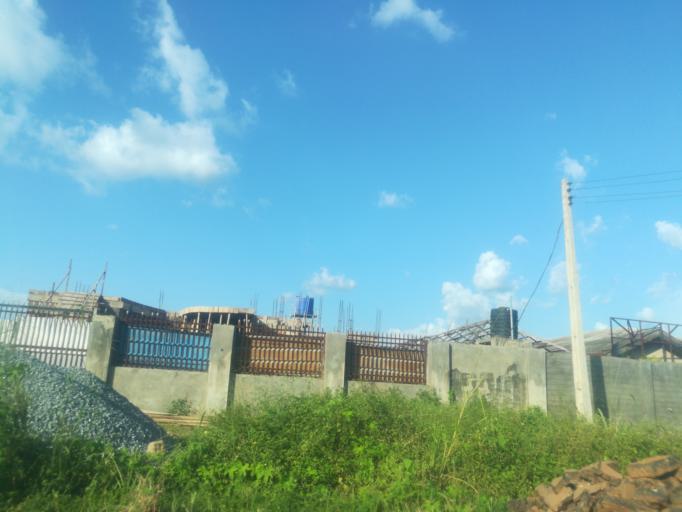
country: NG
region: Oyo
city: Ibadan
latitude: 7.4345
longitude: 3.9748
